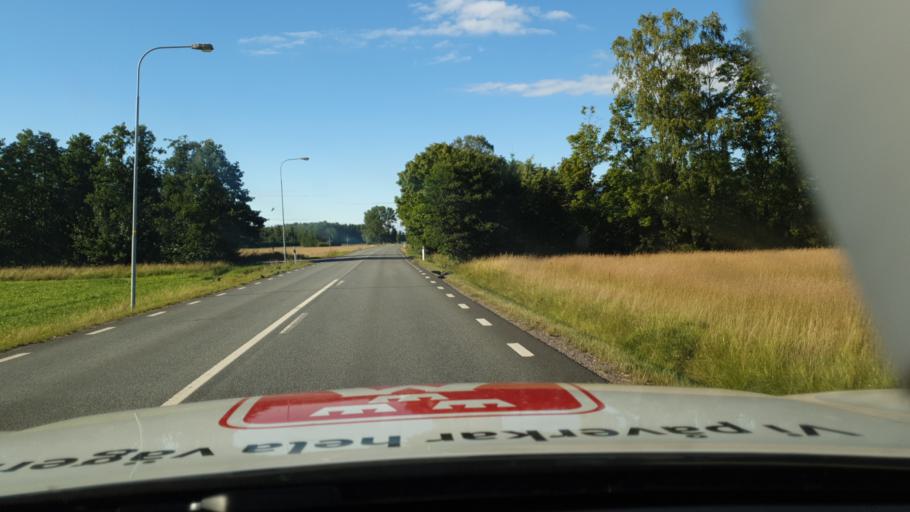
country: SE
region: Vaestra Goetaland
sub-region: Toreboda Kommun
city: Toereboda
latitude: 58.7168
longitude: 14.1321
